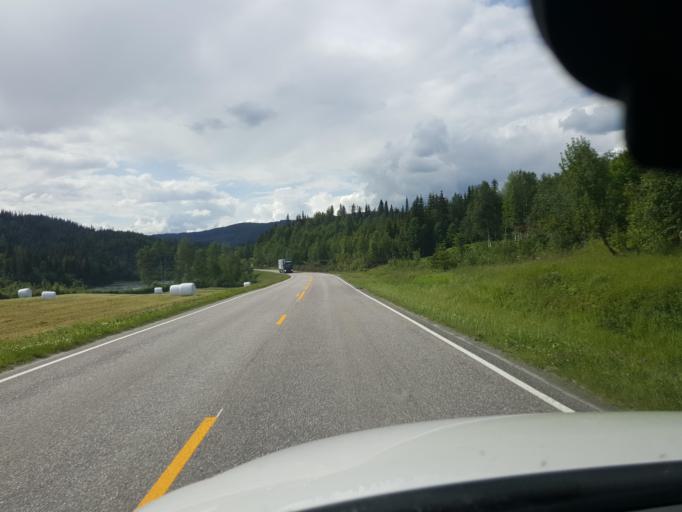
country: NO
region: Nordland
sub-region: Rana
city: Mo i Rana
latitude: 66.4069
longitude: 14.4998
